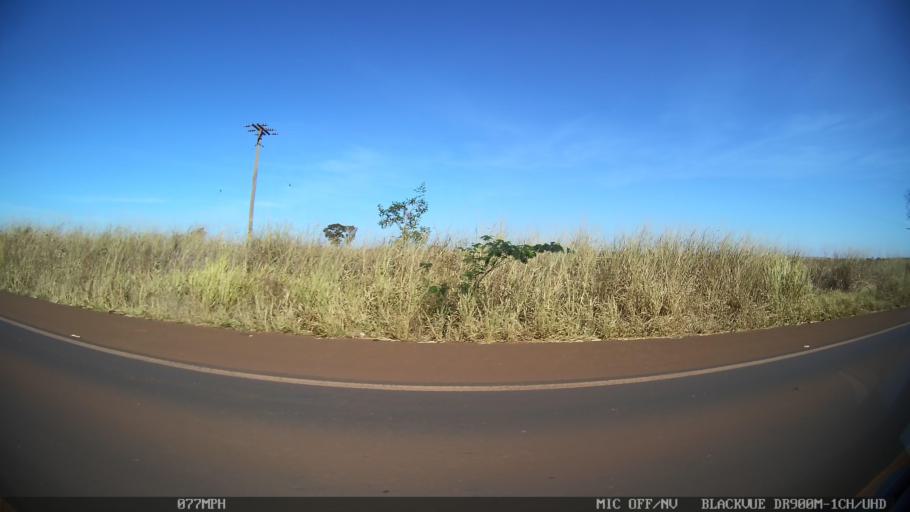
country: BR
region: Sao Paulo
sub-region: Guaira
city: Guaira
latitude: -20.4454
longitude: -48.4010
